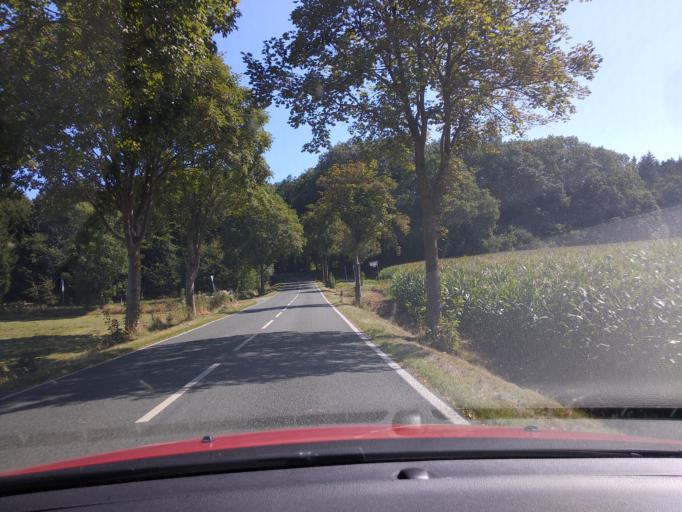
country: DE
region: North Rhine-Westphalia
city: Brakel
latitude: 51.6490
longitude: 9.1437
